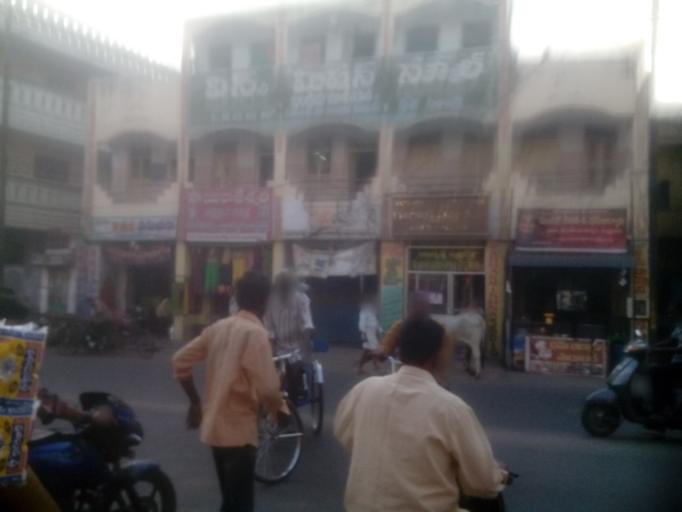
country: IN
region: Andhra Pradesh
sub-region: Krishna
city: Vijayawada
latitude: 16.5278
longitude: 80.6110
